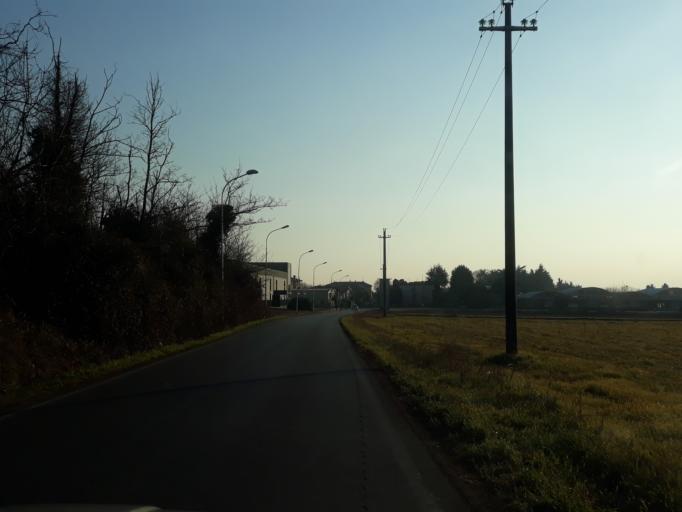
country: IT
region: Lombardy
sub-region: Provincia di Monza e Brianza
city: Bellusco
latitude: 45.6275
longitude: 9.4183
